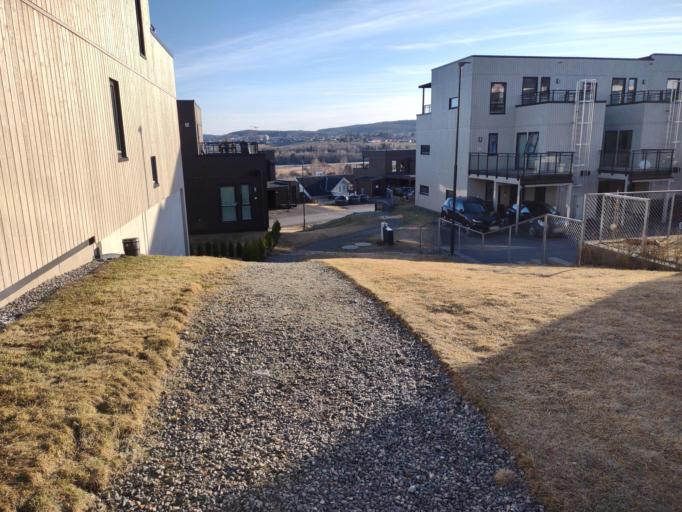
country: NO
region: Akershus
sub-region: Skedsmo
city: Lillestrom
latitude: 59.9765
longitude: 11.0299
